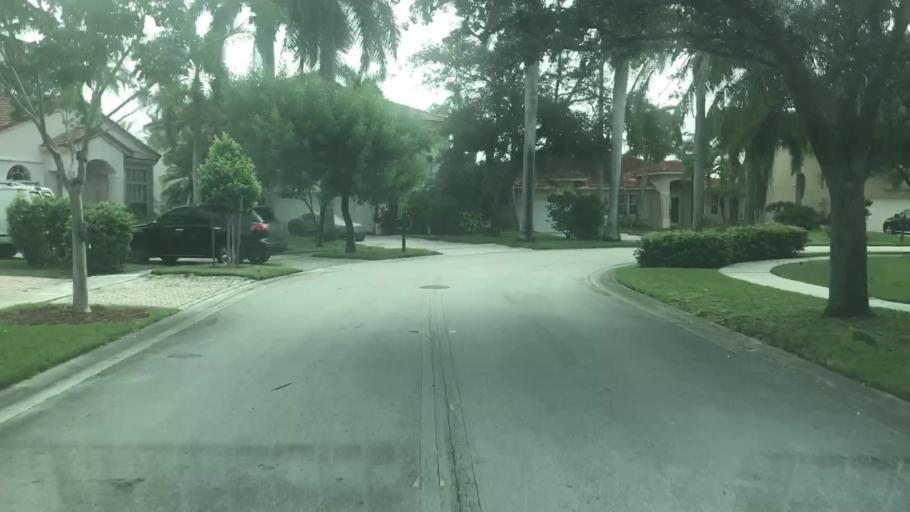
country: US
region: Florida
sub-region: Broward County
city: Southwest Ranches
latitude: 26.0143
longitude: -80.3971
